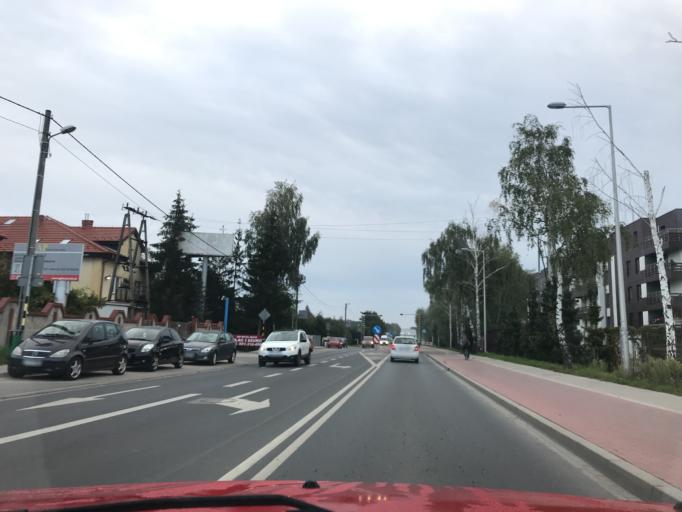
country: PL
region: Greater Poland Voivodeship
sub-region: Powiat poznanski
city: Plewiska
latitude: 52.3942
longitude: 16.7968
